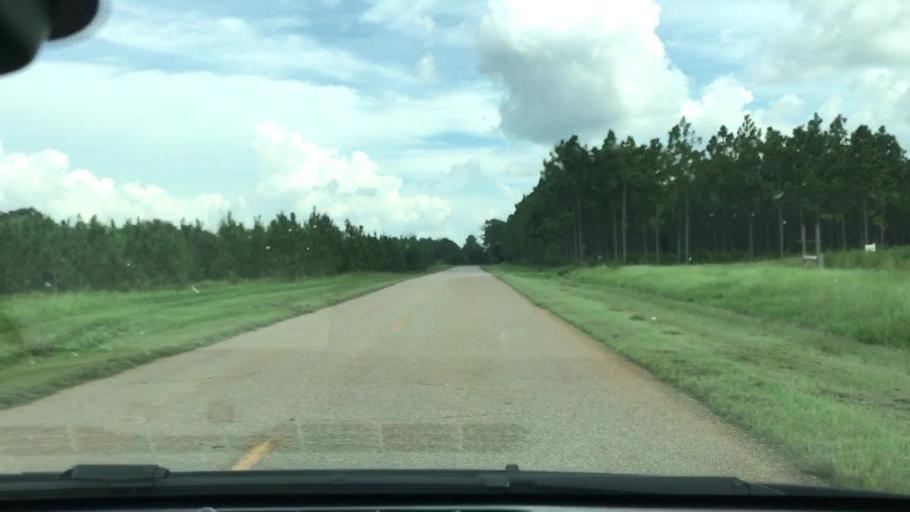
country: US
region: Georgia
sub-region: Clay County
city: Fort Gaines
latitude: 31.5621
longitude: -84.9835
